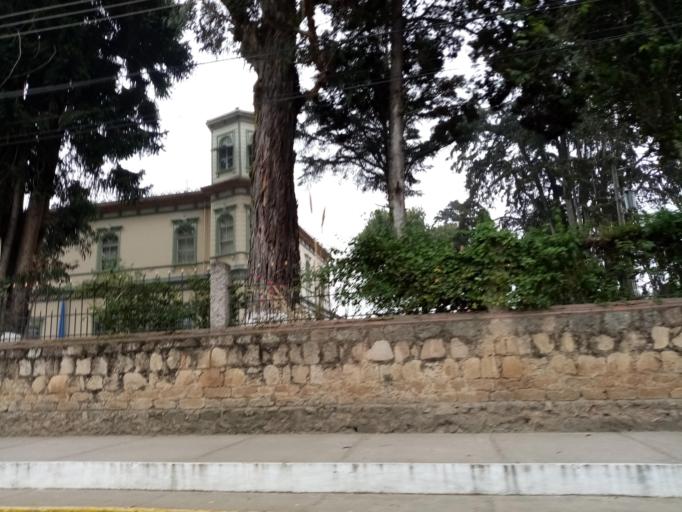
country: GT
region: Quetzaltenango
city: Quetzaltenango
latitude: 14.8449
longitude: -91.5172
